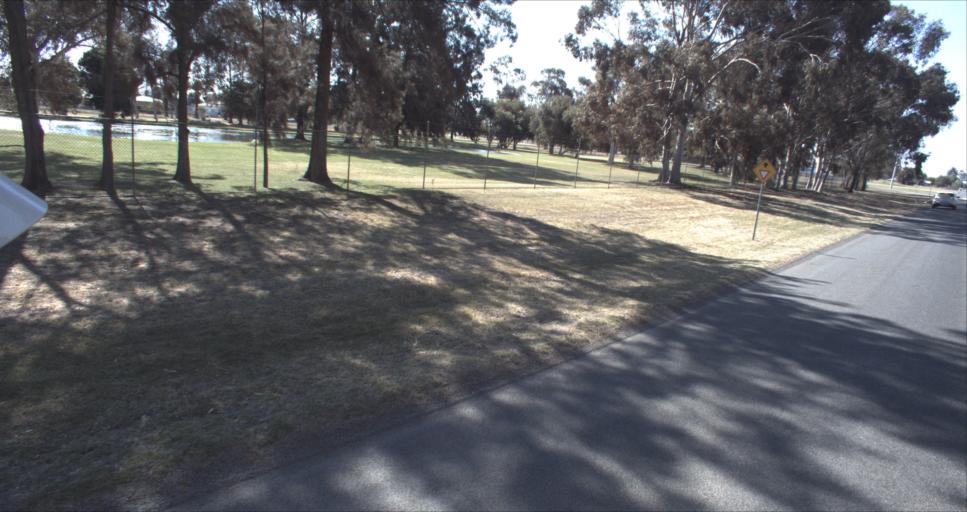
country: AU
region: New South Wales
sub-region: Leeton
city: Leeton
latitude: -34.5648
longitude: 146.4146
